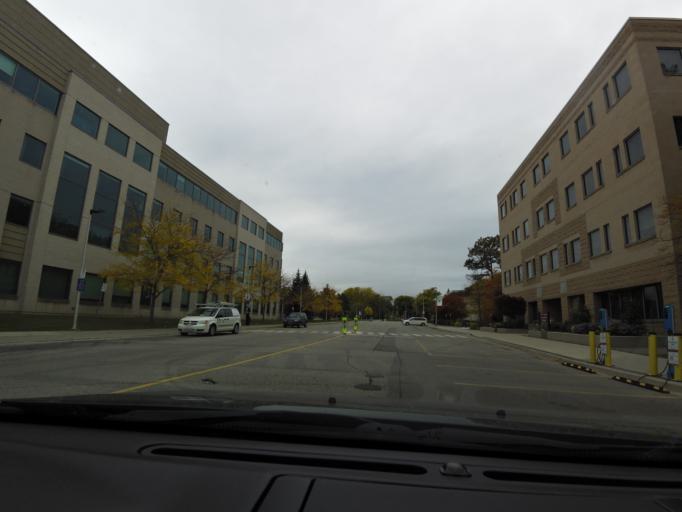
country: CA
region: Ontario
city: Hamilton
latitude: 43.2601
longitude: -79.9205
